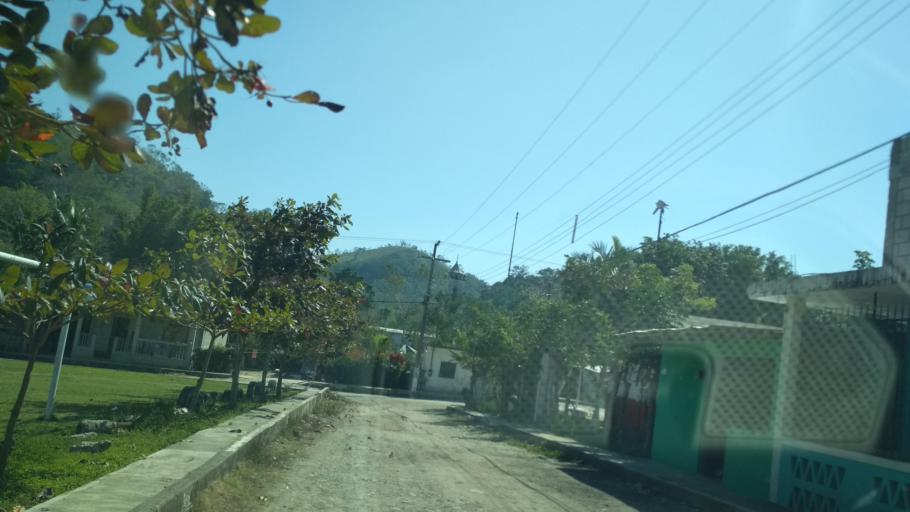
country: MX
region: Veracruz
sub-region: Papantla
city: Polutla
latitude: 20.4777
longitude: -97.2081
